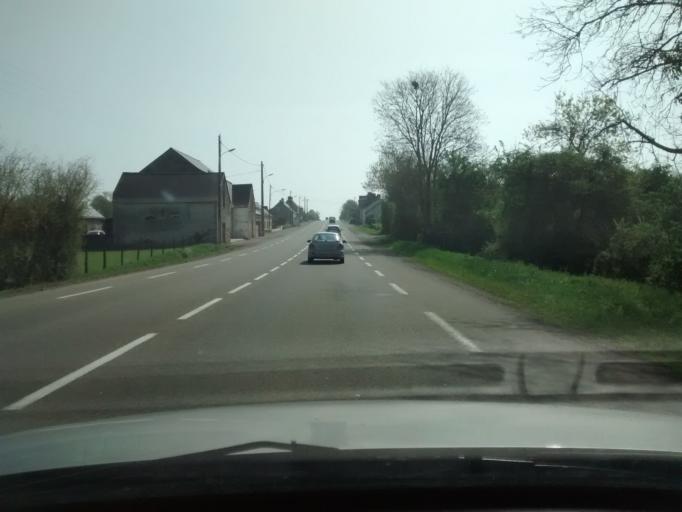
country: FR
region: Pays de la Loire
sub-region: Departement de la Mayenne
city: Soulge-sur-Ouette
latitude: 48.0561
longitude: -0.5567
